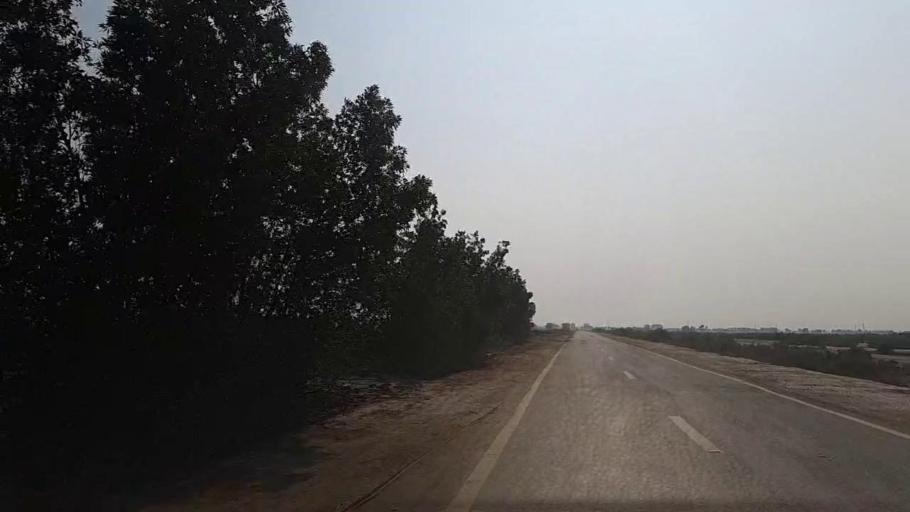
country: PK
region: Sindh
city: Jam Sahib
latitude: 26.3701
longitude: 68.5367
